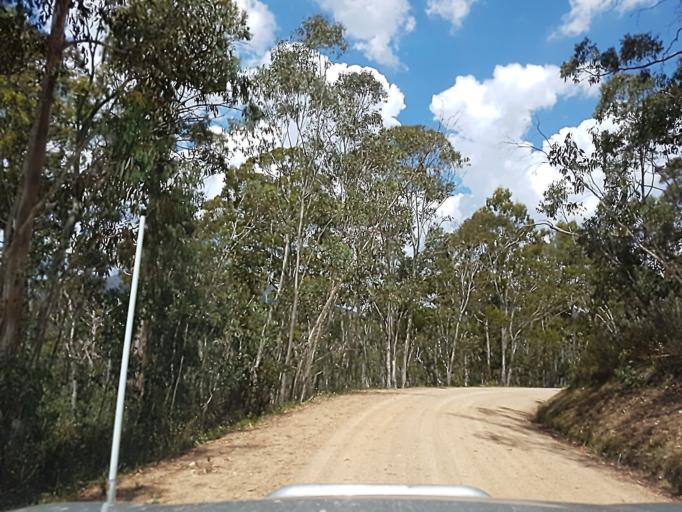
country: AU
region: New South Wales
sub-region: Snowy River
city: Jindabyne
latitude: -36.8834
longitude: 148.0852
